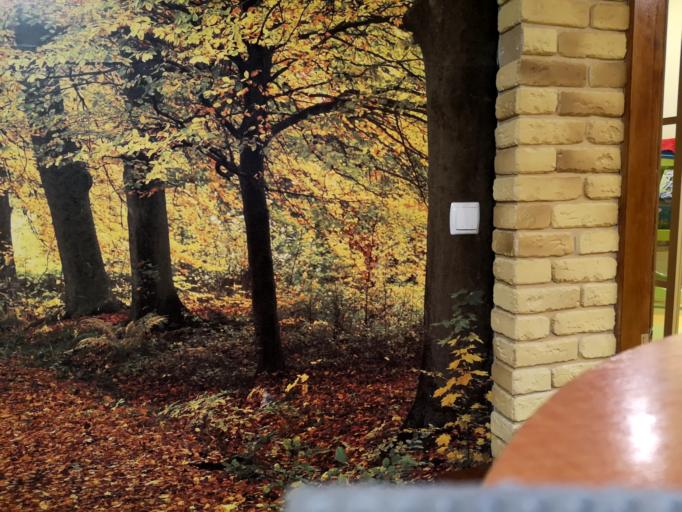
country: RU
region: Sverdlovsk
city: Krasnotur'insk
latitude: 59.9085
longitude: 60.2757
